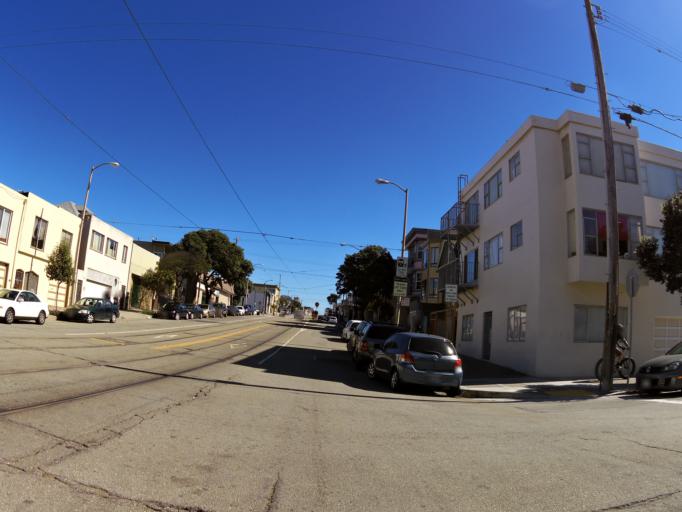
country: US
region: California
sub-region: San Mateo County
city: Daly City
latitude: 37.7604
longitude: -122.5069
